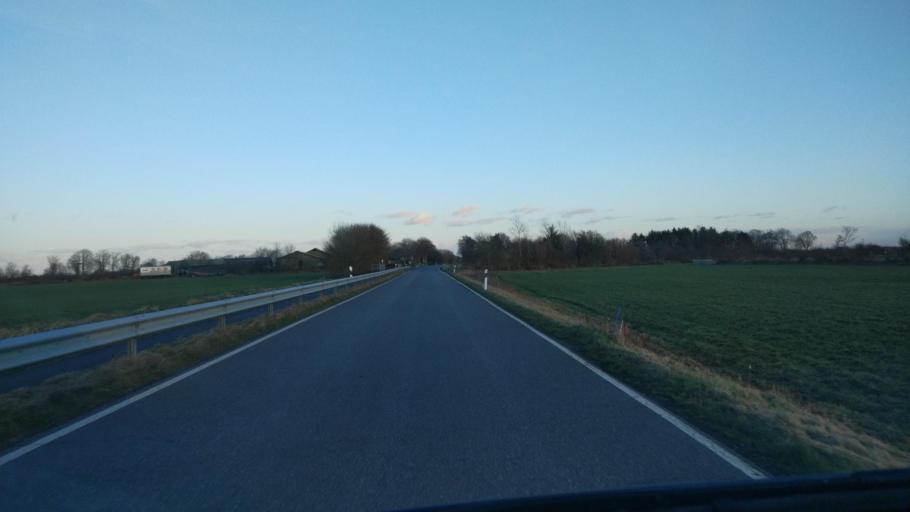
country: DE
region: Schleswig-Holstein
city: Hollingstedt
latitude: 54.4654
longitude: 9.3722
